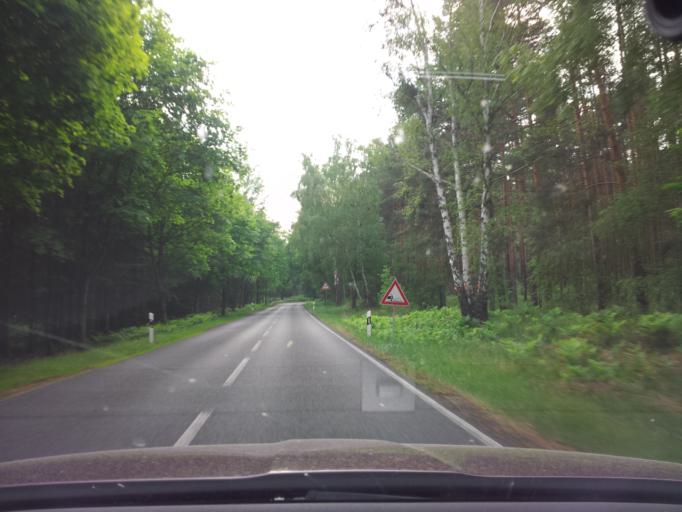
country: DE
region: Brandenburg
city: Beelitz
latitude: 52.2990
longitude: 12.9485
